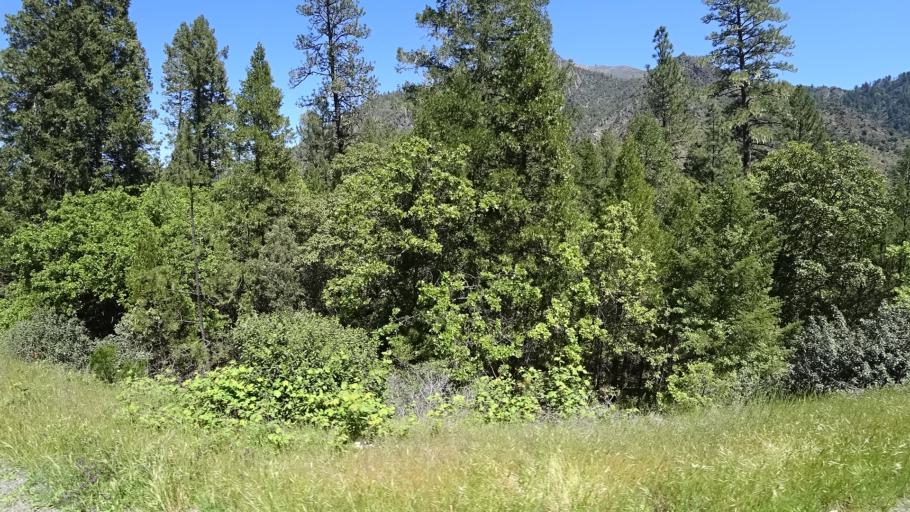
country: US
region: California
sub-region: Humboldt County
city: Willow Creek
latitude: 40.8215
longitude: -123.4830
